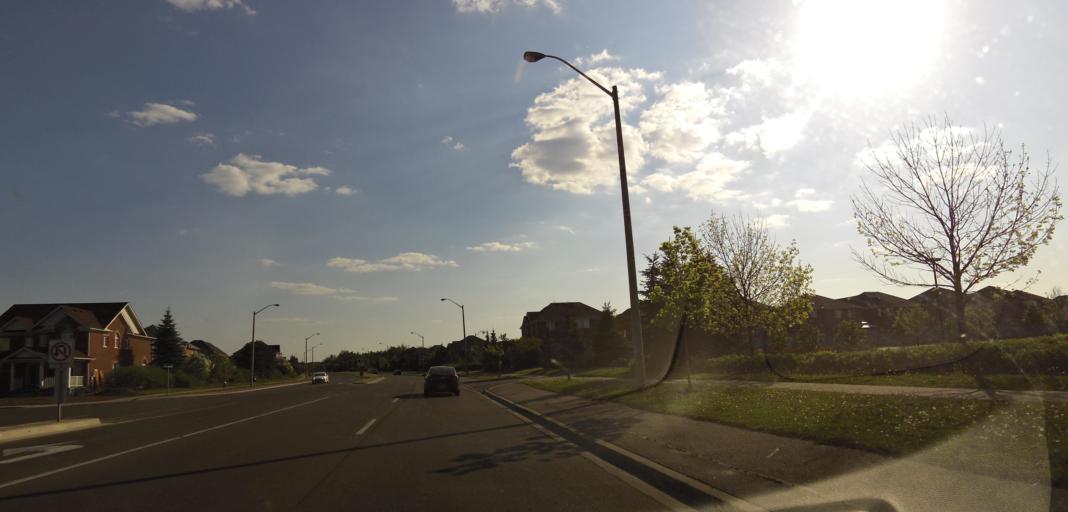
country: CA
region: Ontario
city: Brampton
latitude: 43.7645
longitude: -79.7497
